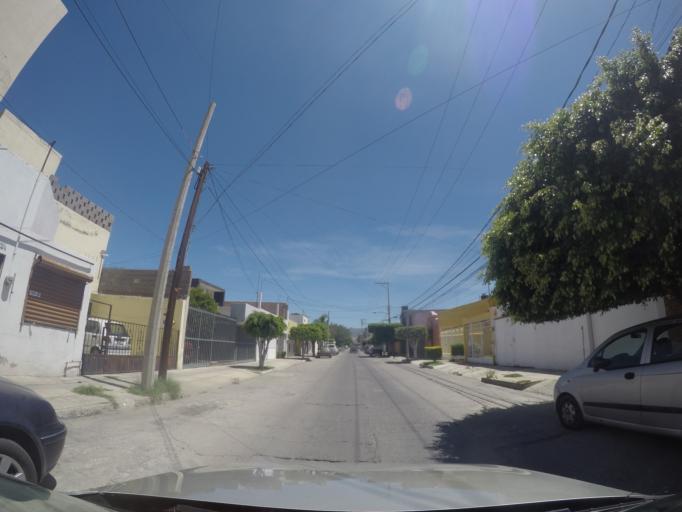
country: MX
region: San Luis Potosi
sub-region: San Luis Potosi
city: San Luis Potosi
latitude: 22.1582
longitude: -100.9902
